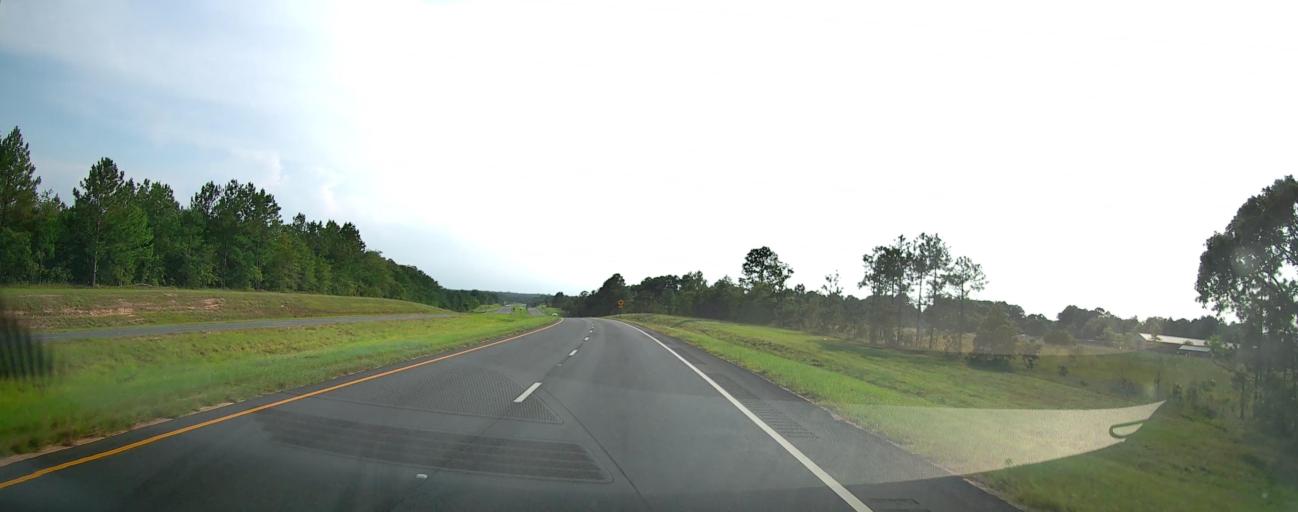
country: US
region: Georgia
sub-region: Taylor County
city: Butler
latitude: 32.5531
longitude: -84.2101
